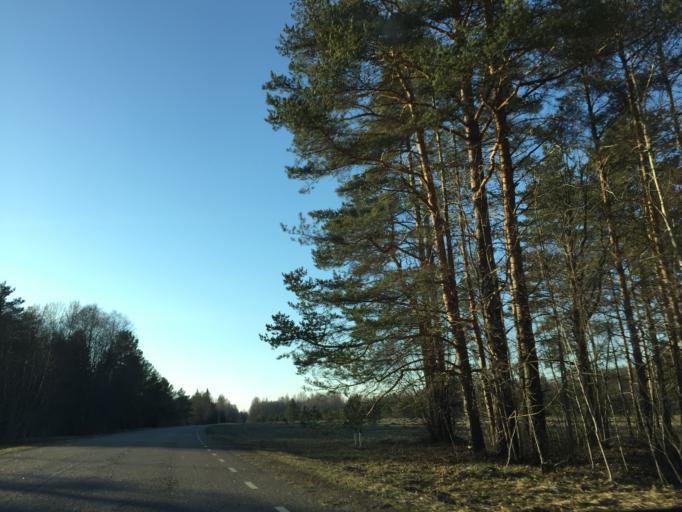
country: EE
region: Ida-Virumaa
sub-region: Sillamaee linn
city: Sillamae
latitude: 59.0851
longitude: 27.6714
